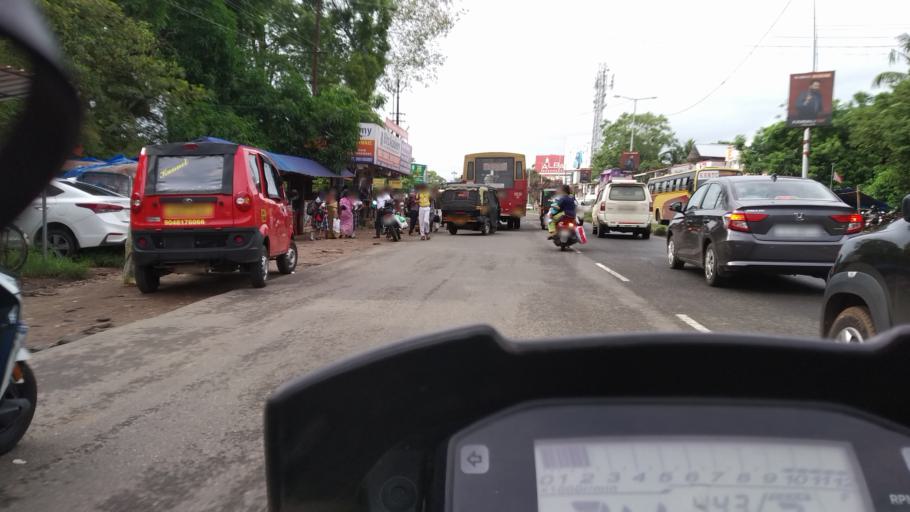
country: IN
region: Kerala
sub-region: Alappuzha
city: Kutiatodu
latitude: 9.7667
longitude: 76.3179
